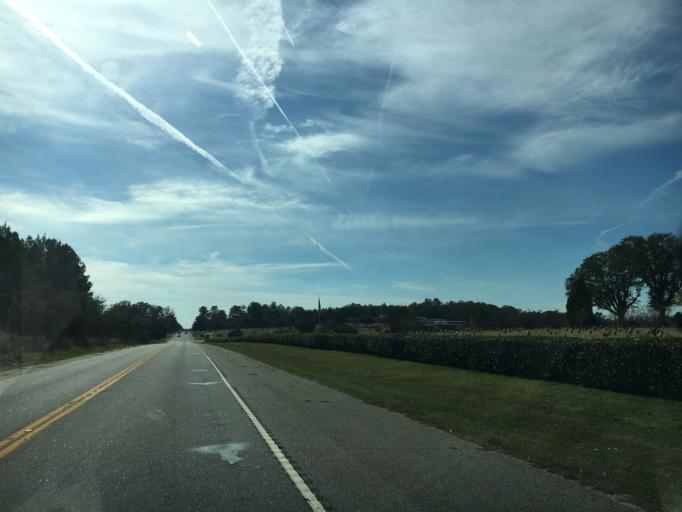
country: US
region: South Carolina
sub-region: Anderson County
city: Anderson
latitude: 34.5397
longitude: -82.5792
